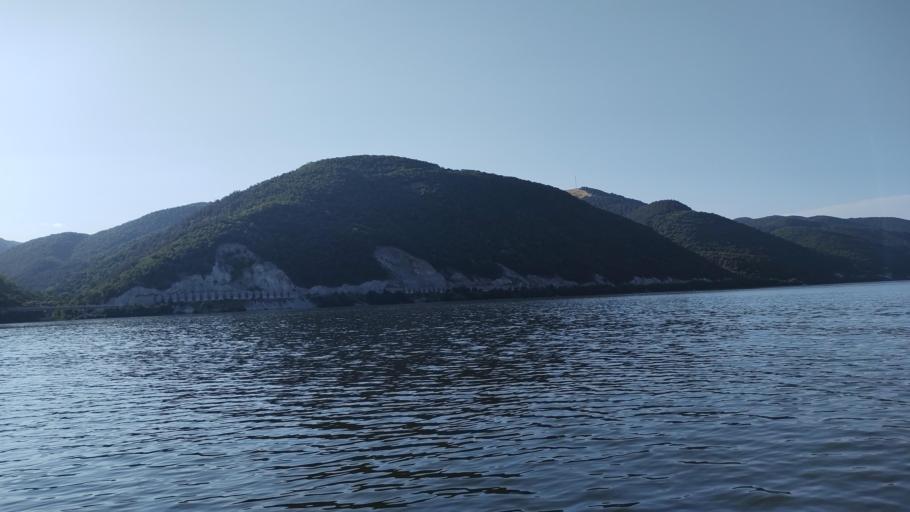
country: RO
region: Mehedinti
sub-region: Comuna Dubova
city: Dubova
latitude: 44.5398
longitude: 22.2189
